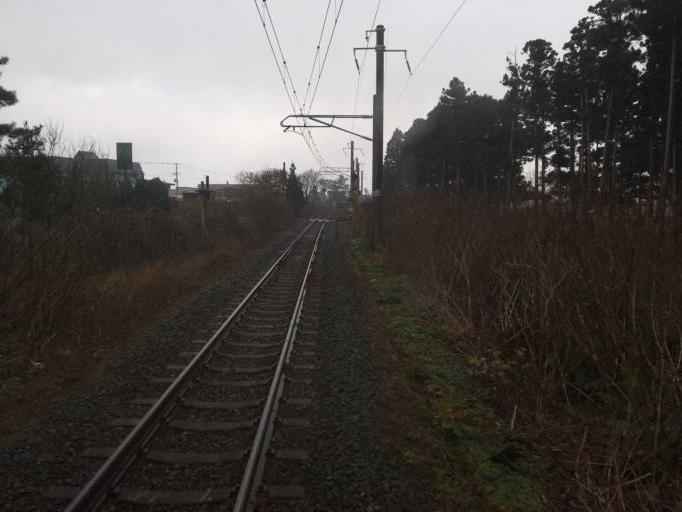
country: JP
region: Aomori
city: Aomori Shi
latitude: 40.9840
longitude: 140.6535
